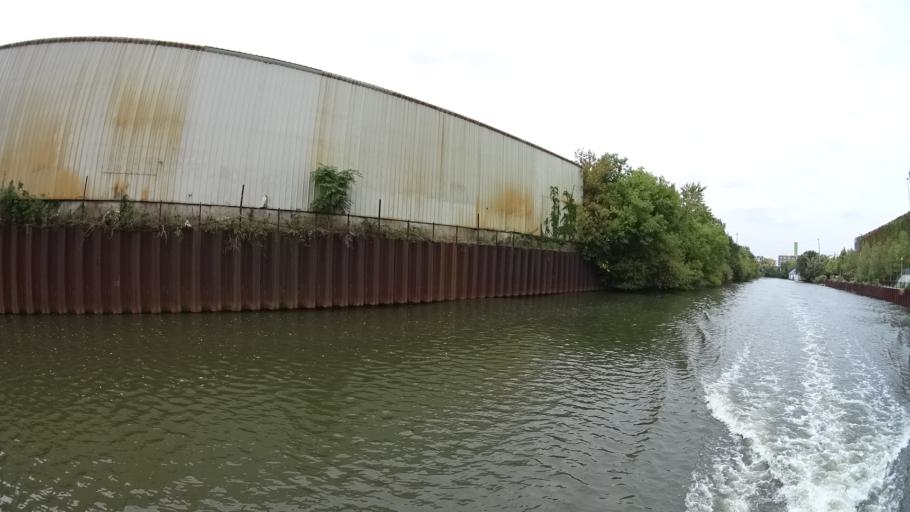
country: US
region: Illinois
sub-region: Cook County
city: Chicago
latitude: 41.9077
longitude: -87.6528
